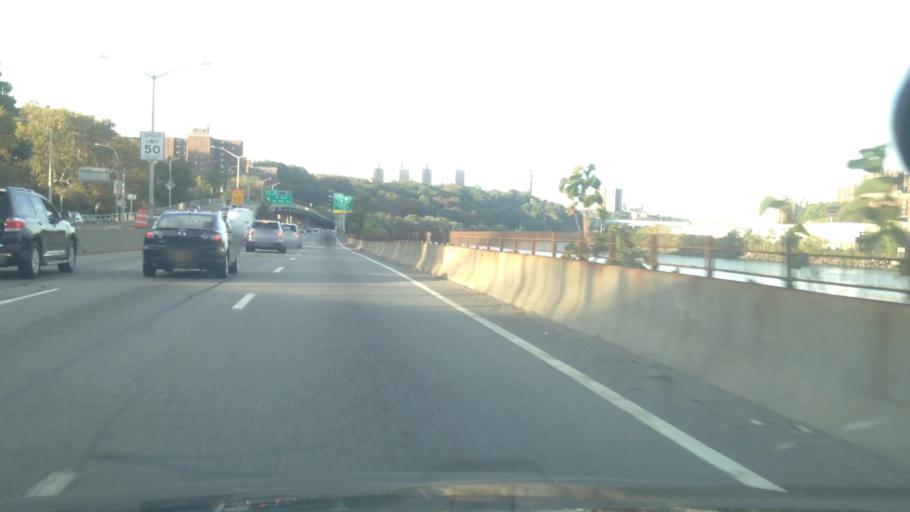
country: US
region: New York
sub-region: New York County
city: Inwood
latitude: 40.8284
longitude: -73.9347
